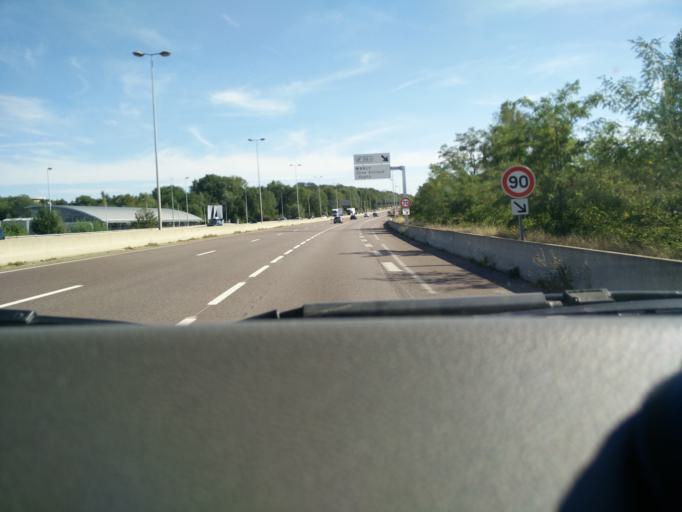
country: FR
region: Lorraine
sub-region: Departement de la Moselle
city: Augny
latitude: 49.0768
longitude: 6.1100
